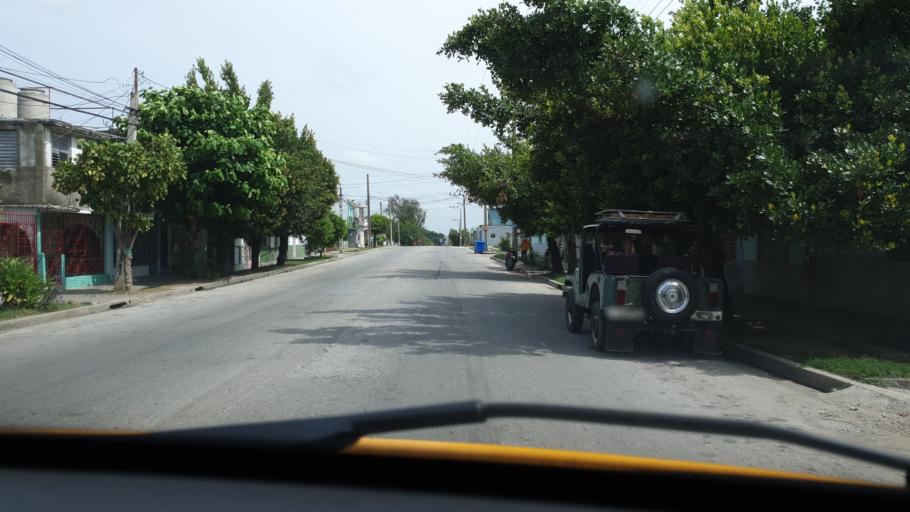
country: CU
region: Villa Clara
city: Santa Clara
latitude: 22.3896
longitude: -79.9599
